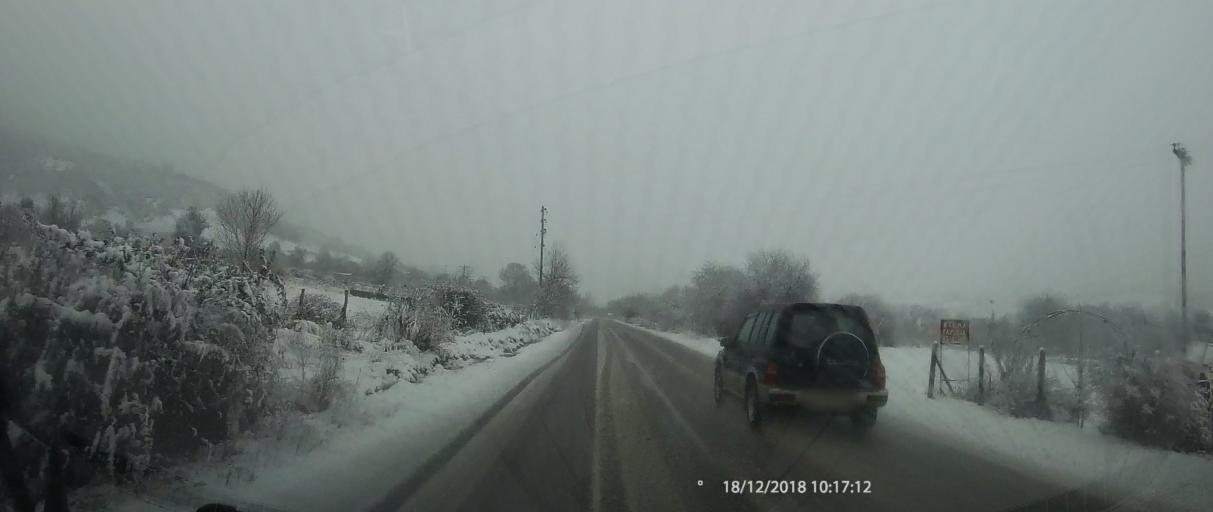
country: GR
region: Thessaly
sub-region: Nomos Larisis
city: Livadi
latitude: 40.1220
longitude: 22.2117
